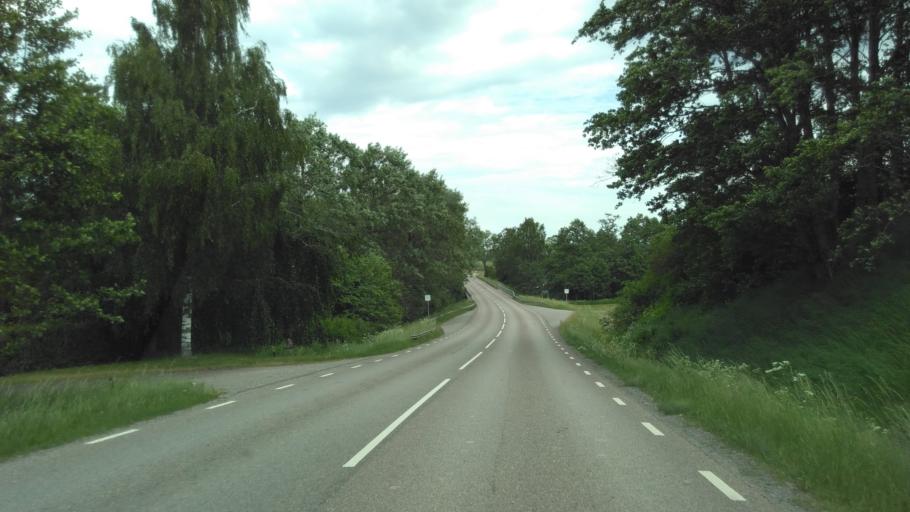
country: SE
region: Vaestra Goetaland
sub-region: Vara Kommun
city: Kvanum
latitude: 58.3991
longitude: 13.1594
